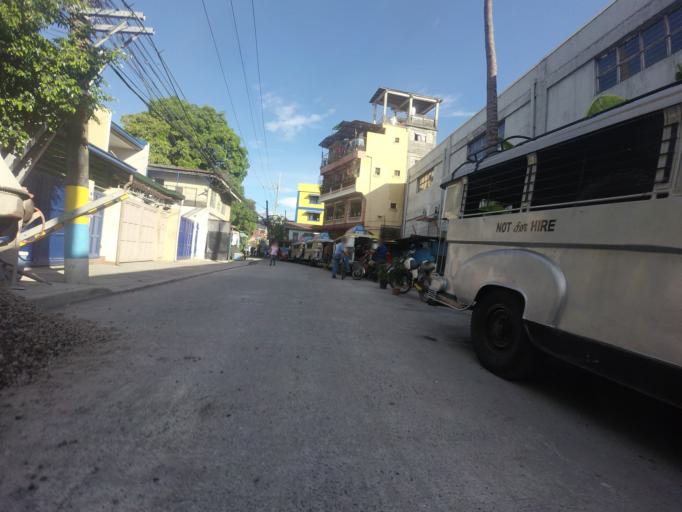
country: PH
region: Metro Manila
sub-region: Mandaluyong
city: Mandaluyong City
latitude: 14.5806
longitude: 121.0270
